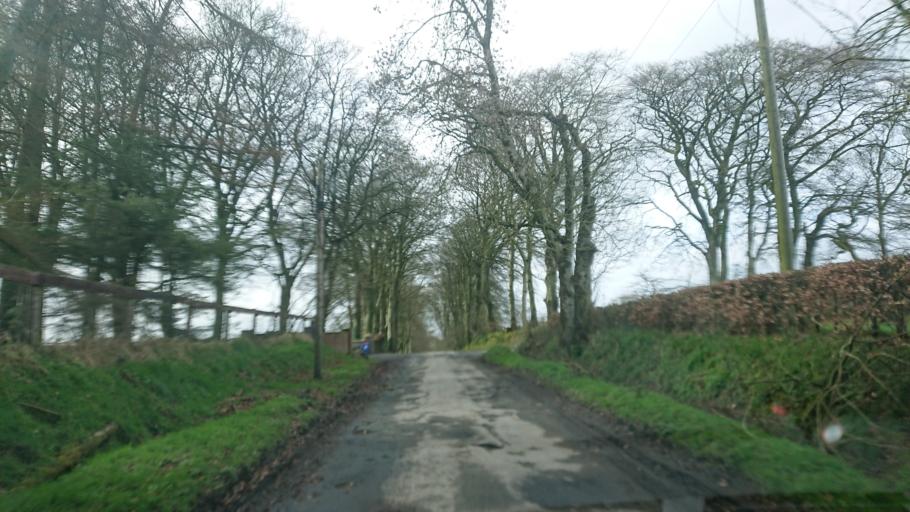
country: IE
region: Leinster
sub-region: Wicklow
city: Blessington
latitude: 53.1575
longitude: -6.5752
